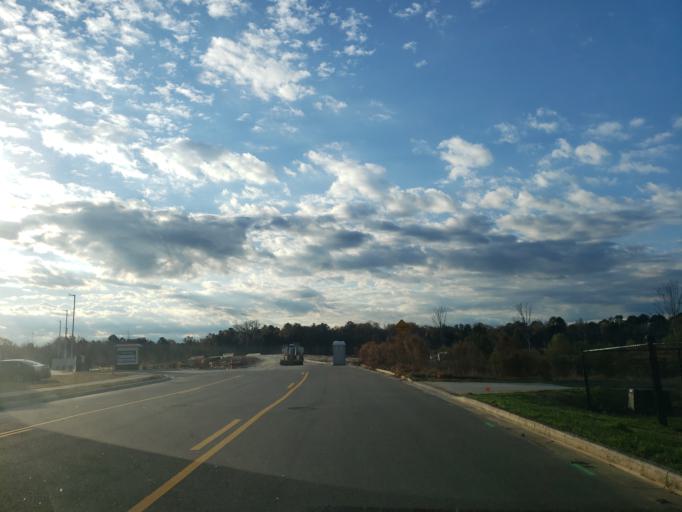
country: US
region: Georgia
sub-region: Chatham County
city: Pooler
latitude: 32.1311
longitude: -81.2481
